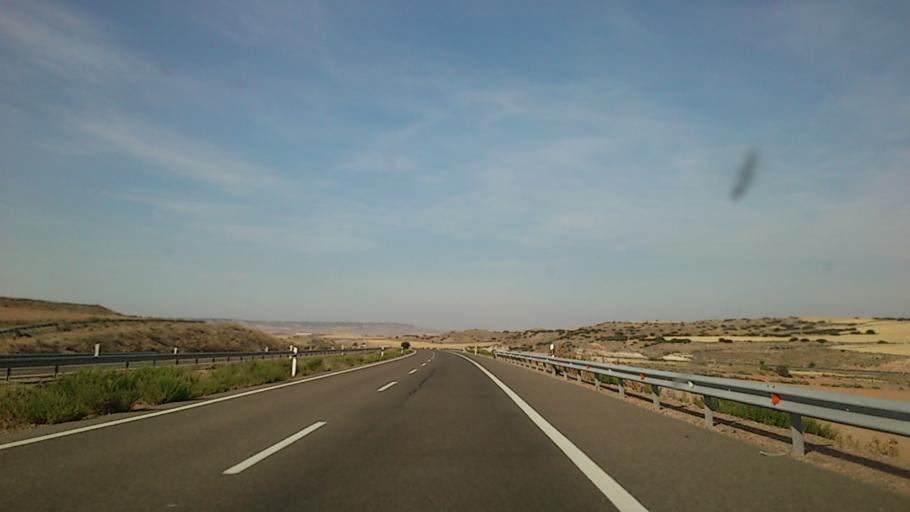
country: ES
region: Aragon
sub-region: Provincia de Zaragoza
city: Longares
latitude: 41.4237
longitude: -1.1512
